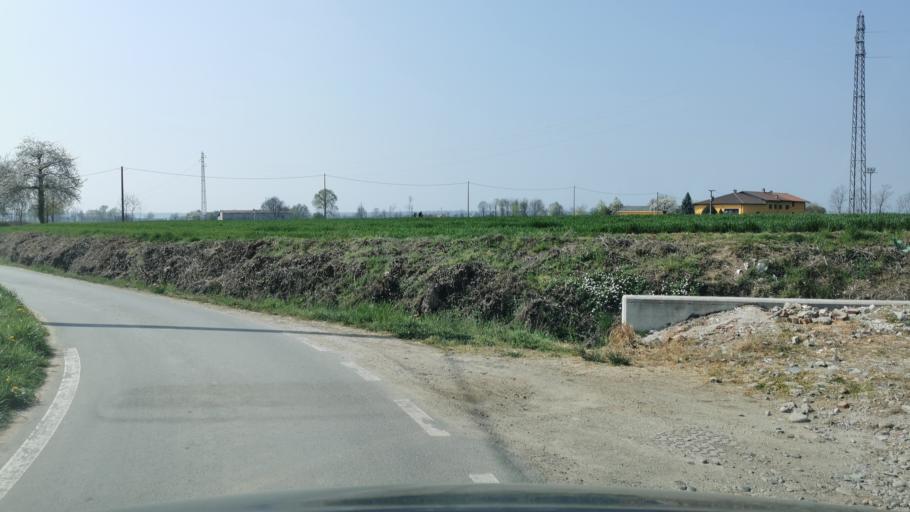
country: IT
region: Piedmont
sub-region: Provincia di Torino
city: Favria
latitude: 45.3230
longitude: 7.7037
